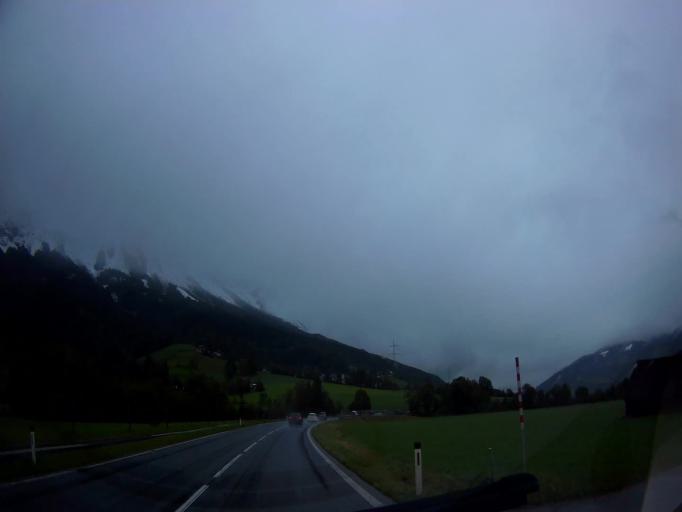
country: AT
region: Styria
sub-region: Politischer Bezirk Liezen
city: Sankt Martin am Grimming
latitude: 47.4849
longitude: 13.9703
